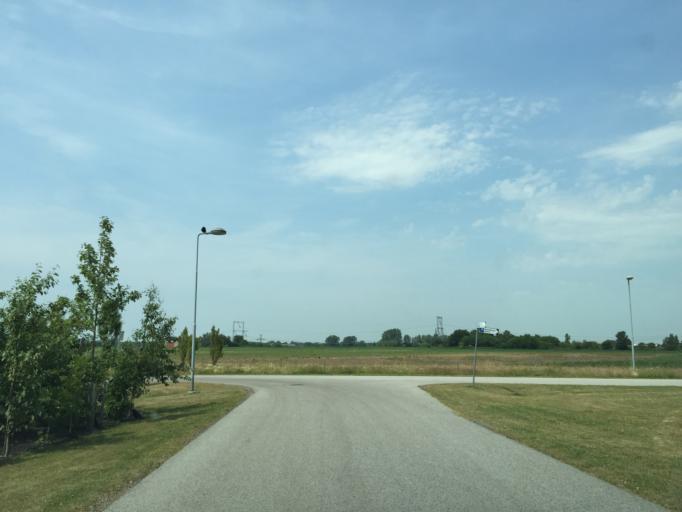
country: SE
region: Skane
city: Bjarred
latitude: 55.7334
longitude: 13.0232
